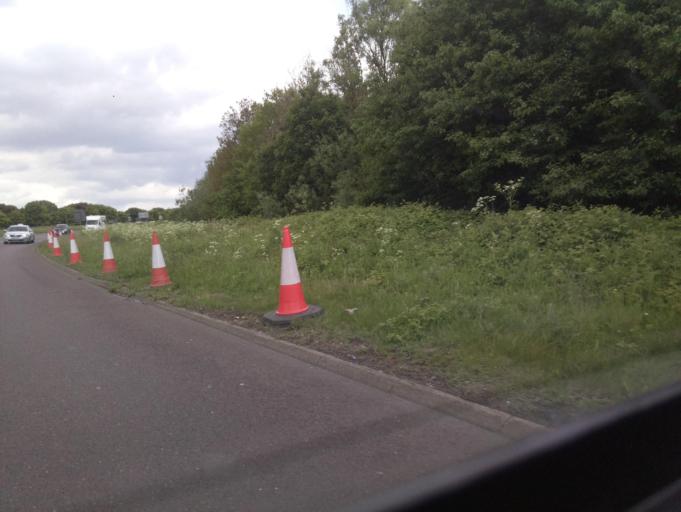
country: GB
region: England
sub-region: County Durham
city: Chester-le-Street
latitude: 54.9027
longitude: -1.5640
